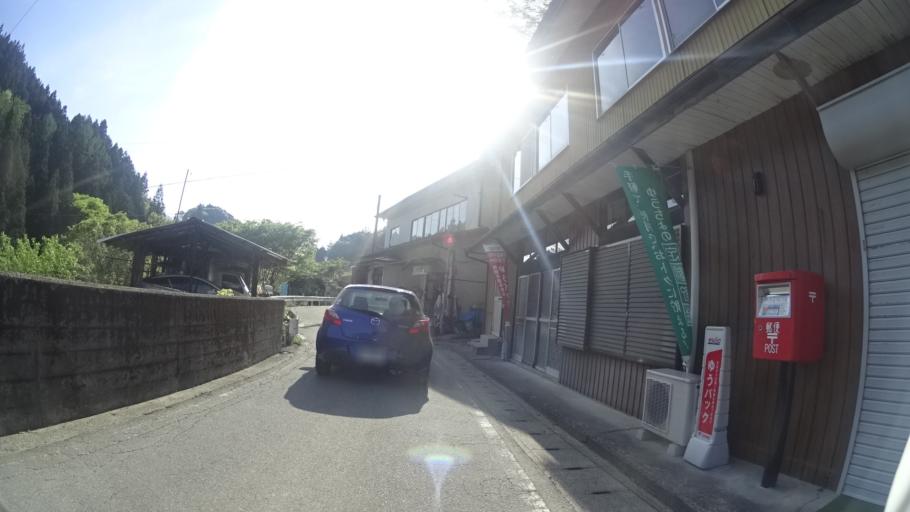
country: JP
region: Tokushima
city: Ikedacho
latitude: 33.8746
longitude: 133.9897
